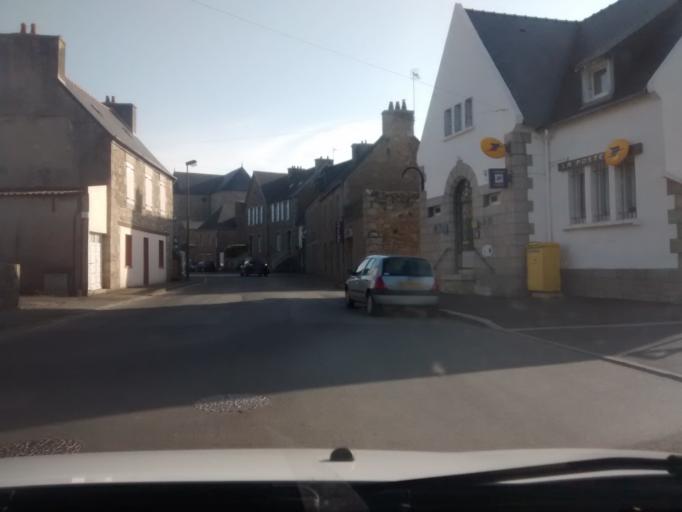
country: FR
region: Brittany
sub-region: Departement des Cotes-d'Armor
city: Penvenan
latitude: 48.8132
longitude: -3.2952
